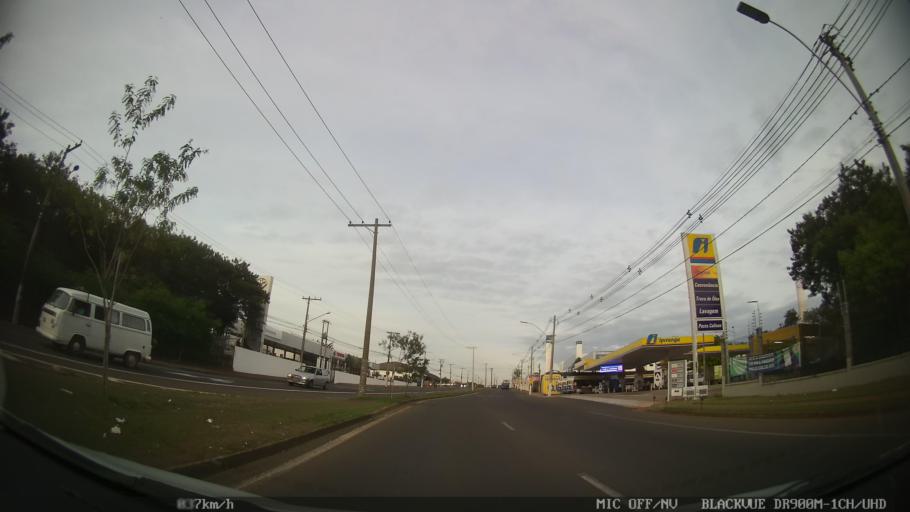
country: BR
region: Sao Paulo
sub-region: Limeira
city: Limeira
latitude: -22.5875
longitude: -47.3904
